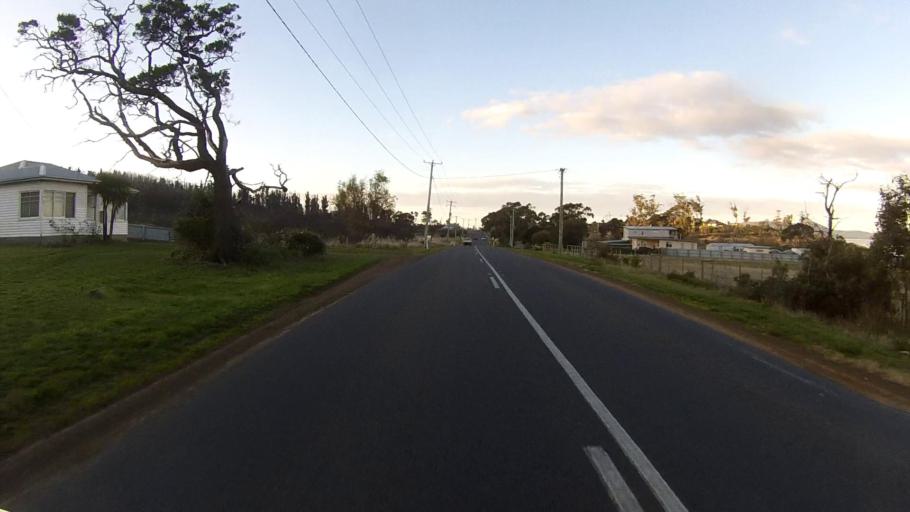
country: AU
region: Tasmania
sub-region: Sorell
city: Sorell
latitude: -42.8810
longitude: 147.8186
